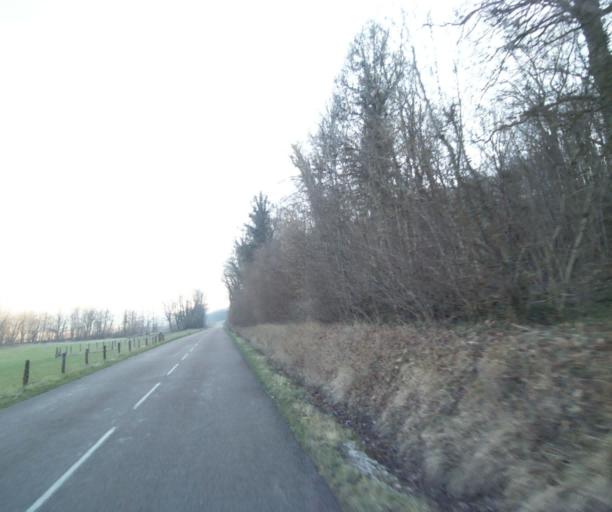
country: FR
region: Champagne-Ardenne
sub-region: Departement de la Haute-Marne
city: Bienville
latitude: 48.5654
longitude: 5.0802
